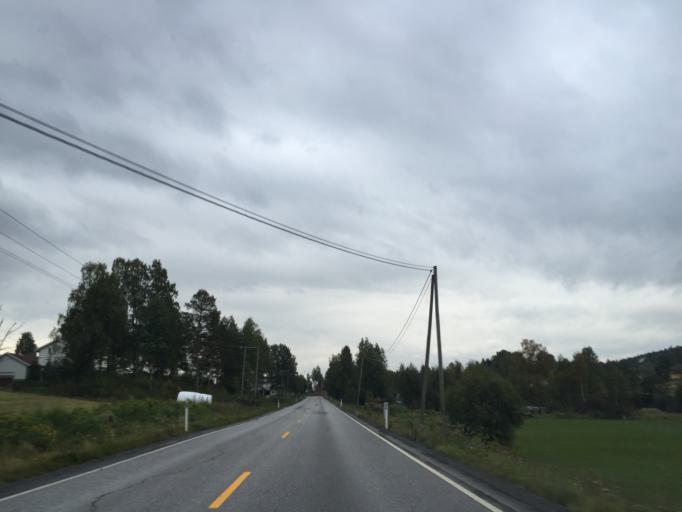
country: NO
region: Hedmark
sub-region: Nord-Odal
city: Sand
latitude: 60.3968
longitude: 11.5284
